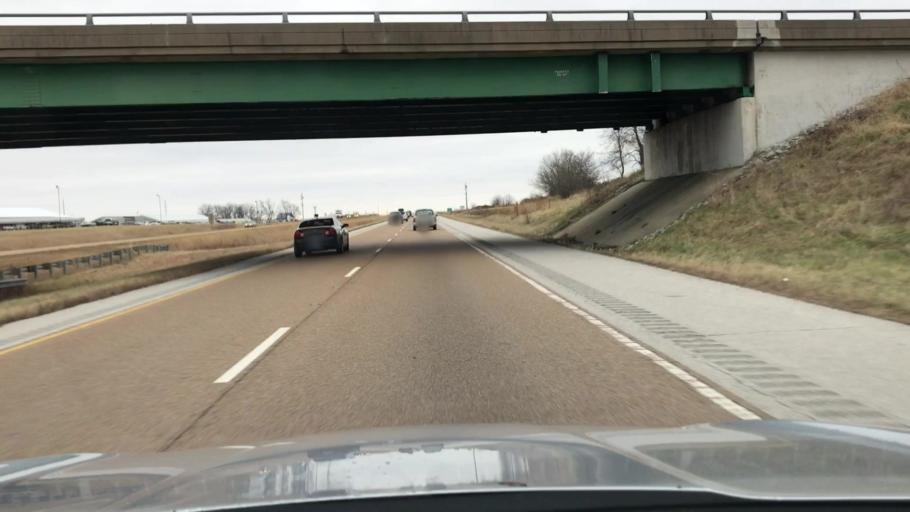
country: US
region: Illinois
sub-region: Macoupin County
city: Staunton
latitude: 39.0321
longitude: -89.7537
